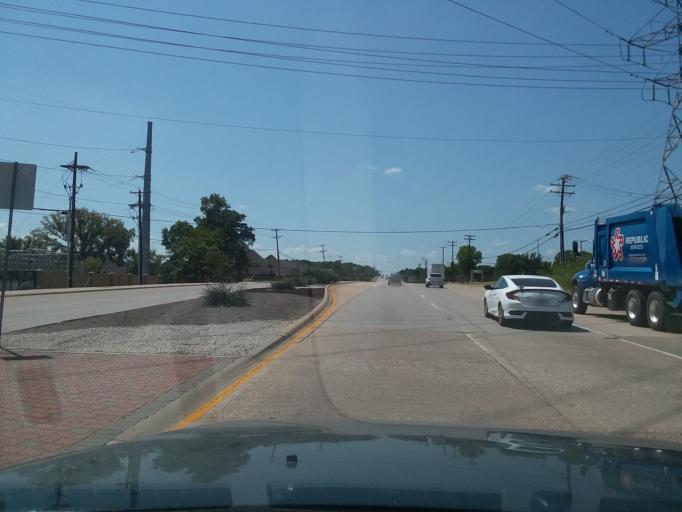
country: US
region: Texas
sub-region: Tarrant County
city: Euless
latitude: 32.8655
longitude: -97.0999
